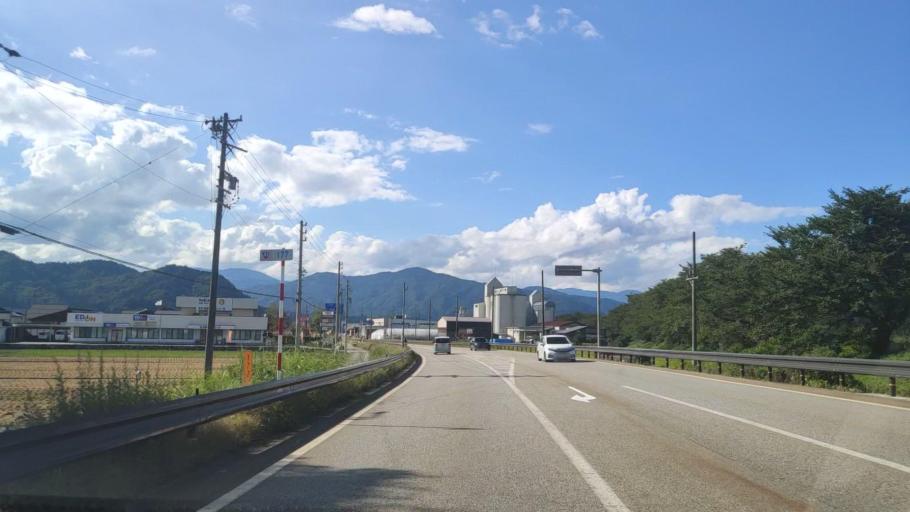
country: JP
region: Gifu
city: Takayama
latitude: 36.2455
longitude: 137.1699
